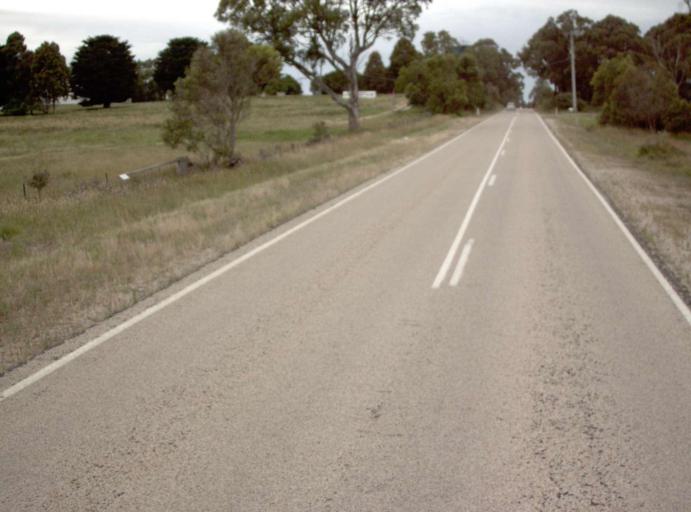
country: AU
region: Victoria
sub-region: East Gippsland
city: Bairnsdale
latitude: -37.8786
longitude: 147.5594
